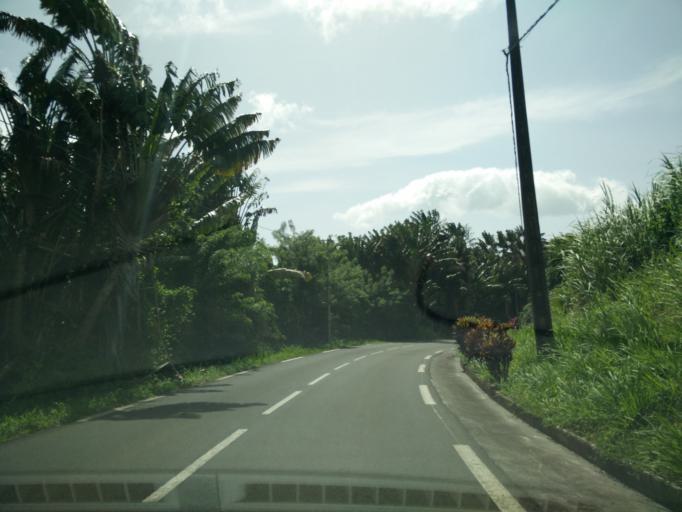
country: MQ
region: Martinique
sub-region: Martinique
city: Le Morne-Rouge
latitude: 14.7618
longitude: -61.1540
